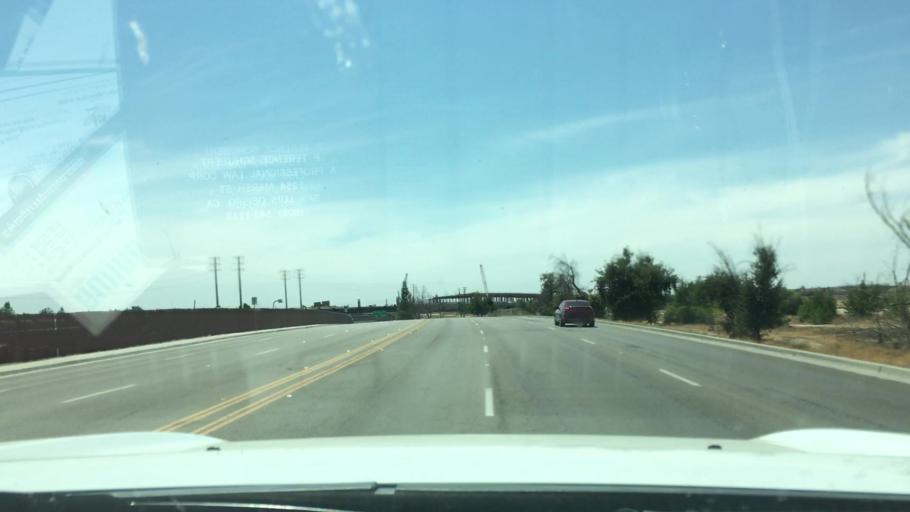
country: US
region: California
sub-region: Kern County
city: Bakersfield
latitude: 35.3729
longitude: -119.0510
